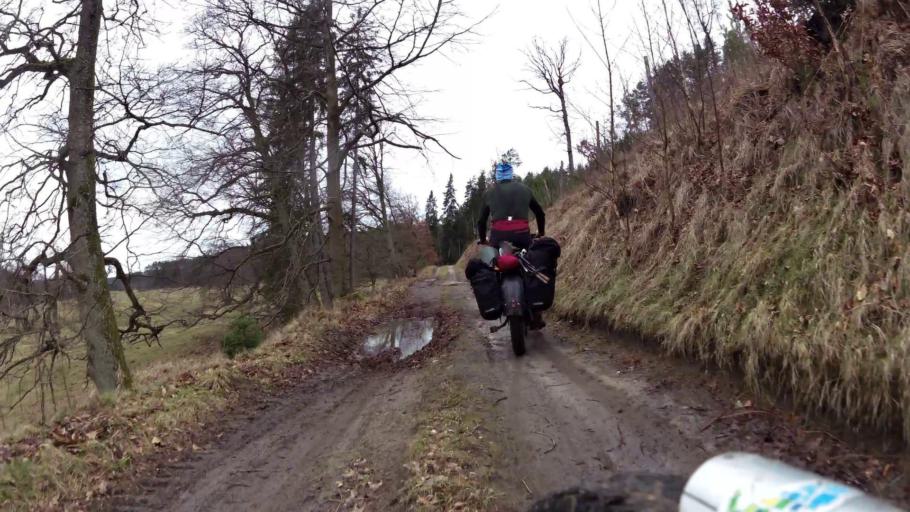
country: PL
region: Pomeranian Voivodeship
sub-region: Powiat bytowski
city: Kolczyglowy
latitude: 54.2505
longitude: 17.2980
